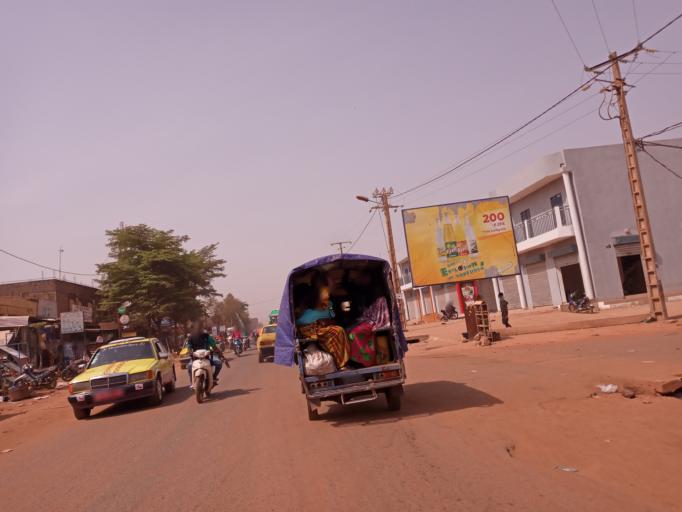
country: ML
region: Bamako
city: Bamako
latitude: 12.5935
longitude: -7.9628
